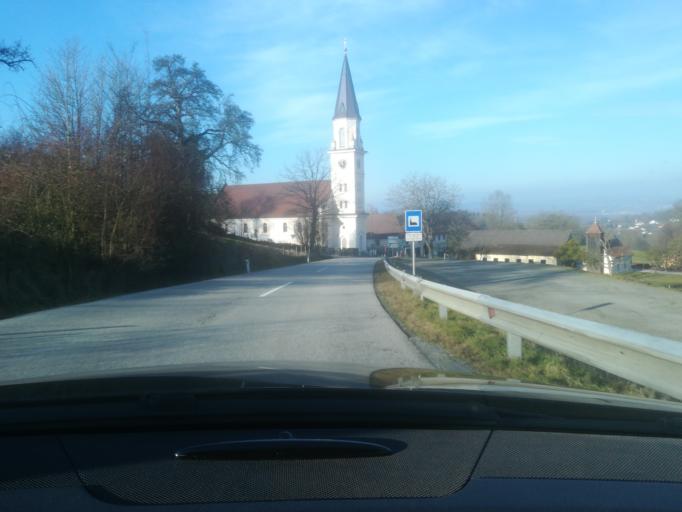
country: AT
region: Upper Austria
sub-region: Wels-Land
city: Buchkirchen
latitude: 48.2488
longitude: 14.0488
